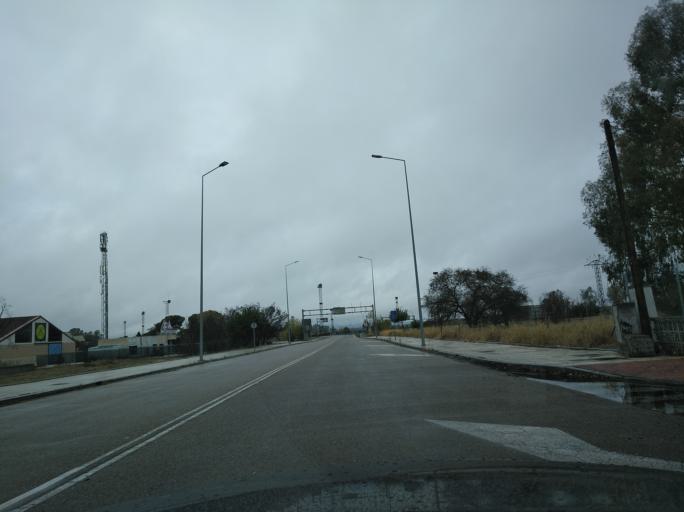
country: ES
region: Extremadura
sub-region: Provincia de Badajoz
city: Badajoz
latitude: 38.8835
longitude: -7.0274
